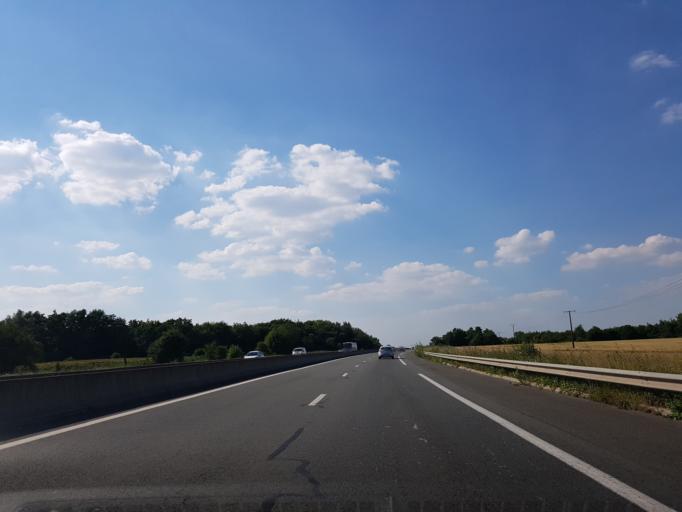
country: FR
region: Nord-Pas-de-Calais
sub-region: Departement du Nord
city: Abscon
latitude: 50.3351
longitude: 3.3218
